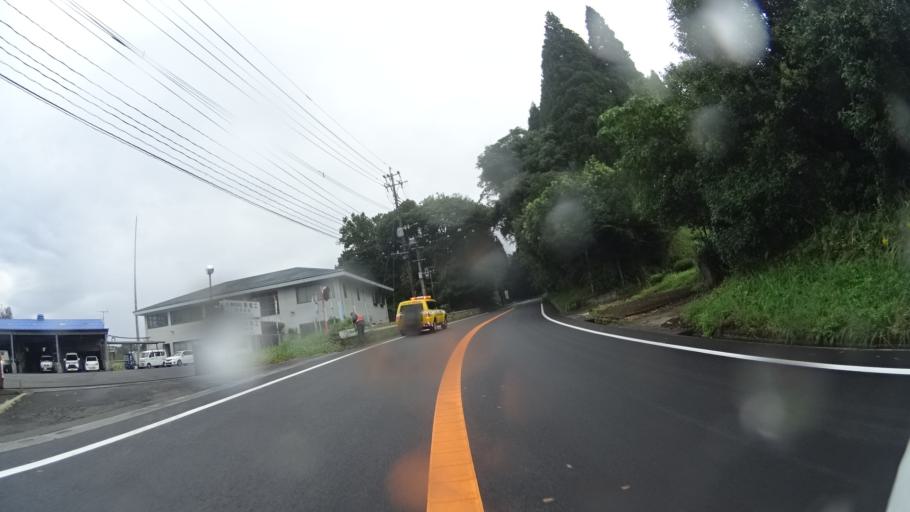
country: JP
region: Kagoshima
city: Kajiki
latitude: 31.7824
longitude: 130.6737
